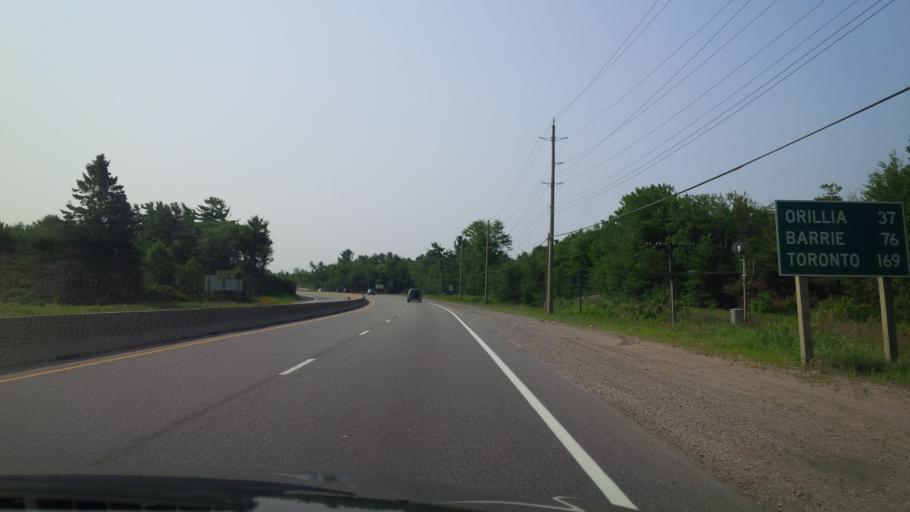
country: CA
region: Ontario
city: Gravenhurst
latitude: 44.8999
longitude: -79.3655
